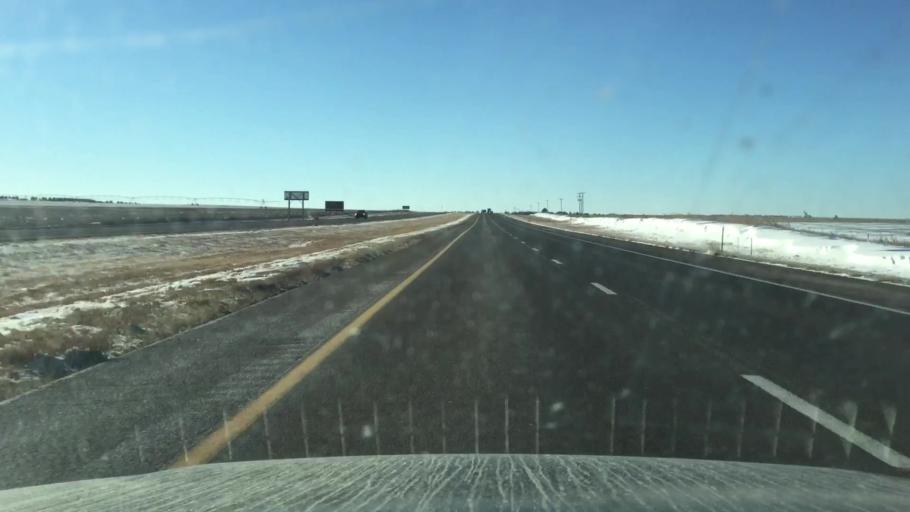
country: US
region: Kansas
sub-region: Thomas County
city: Colby
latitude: 39.3652
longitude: -101.1141
